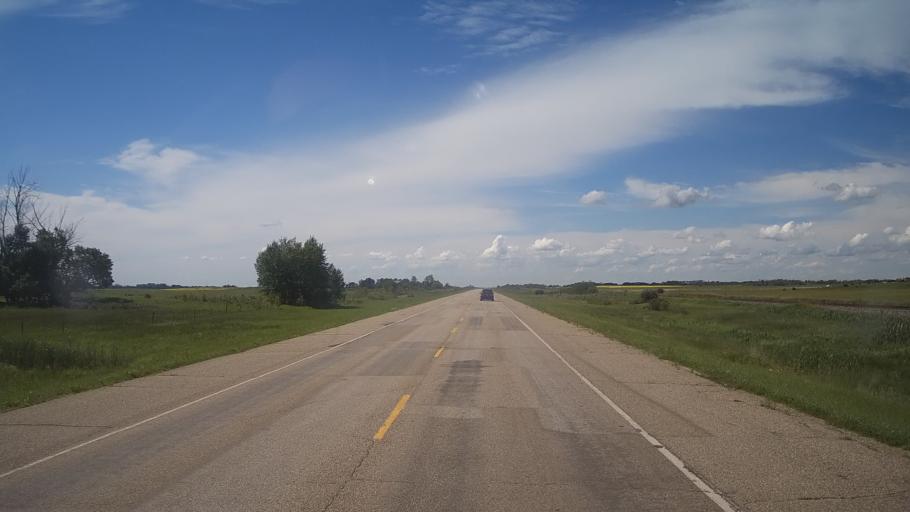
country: CA
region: Saskatchewan
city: Yorkton
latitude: 51.0677
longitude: -102.2195
